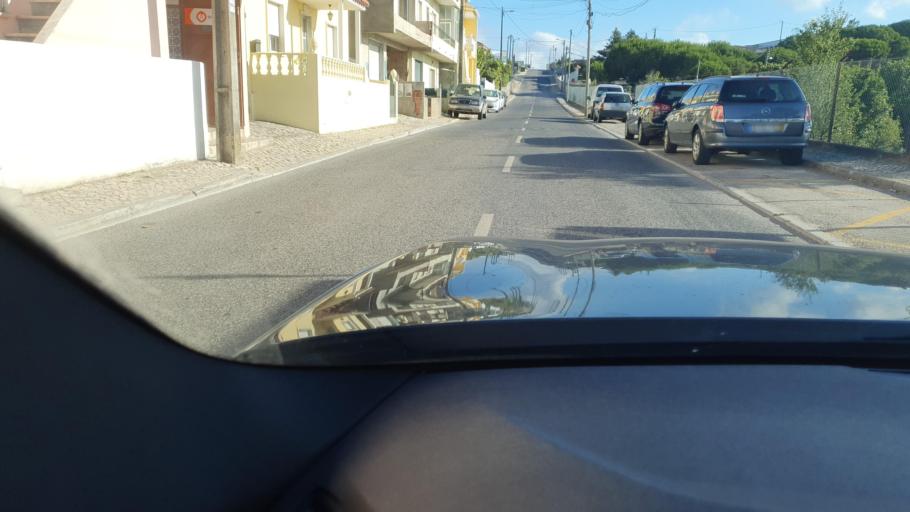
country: PT
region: Lisbon
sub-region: Sintra
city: Belas
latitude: 38.7981
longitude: -9.2533
